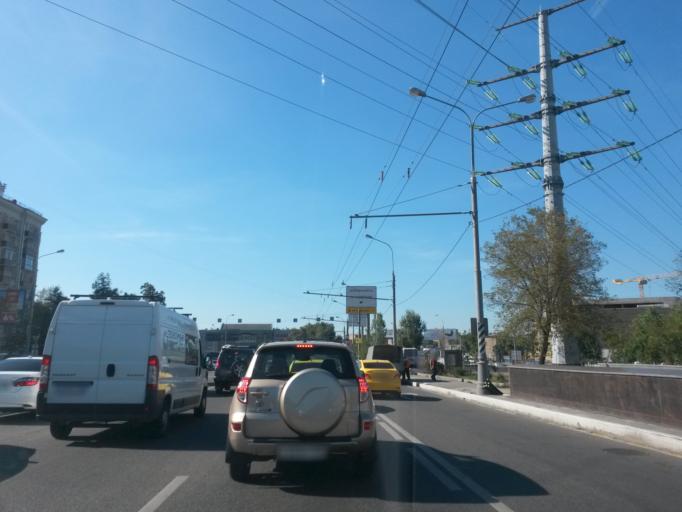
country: RU
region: Moscow
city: Nagornyy
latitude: 55.6620
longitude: 37.6339
